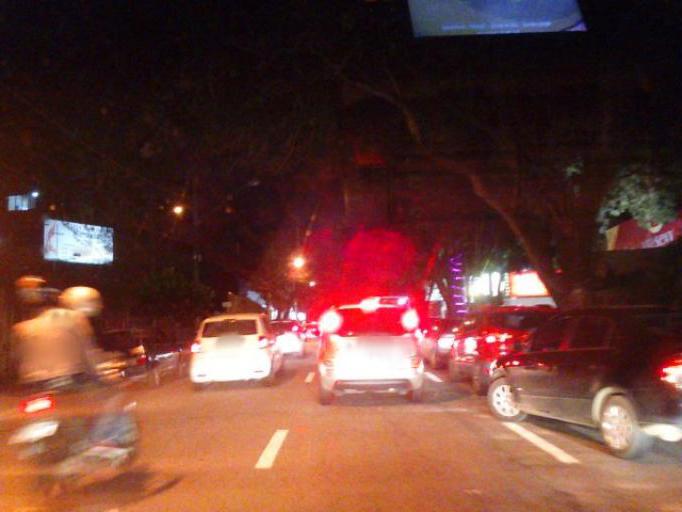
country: BR
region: Sao Paulo
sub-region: Sao Jose Dos Campos
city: Sao Jose dos Campos
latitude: -23.2039
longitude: -45.8935
